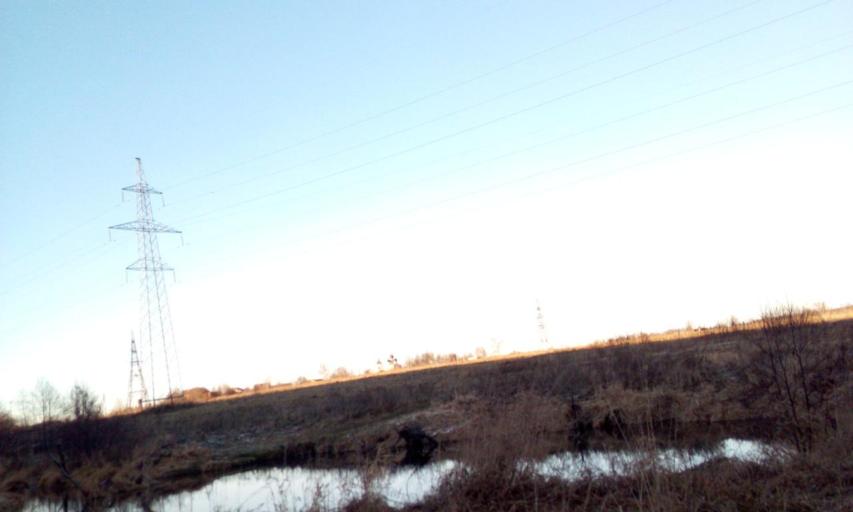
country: RU
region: Moskovskaya
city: Selyatino
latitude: 55.5343
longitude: 37.0018
